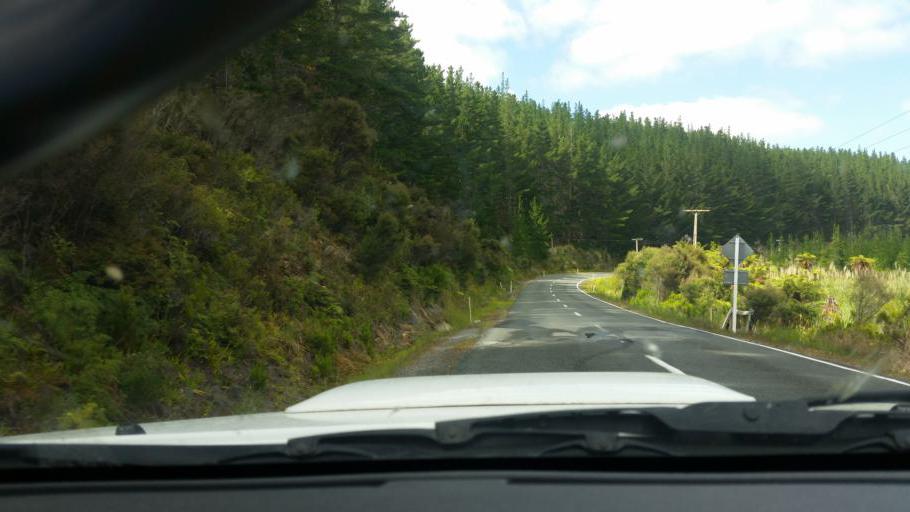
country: NZ
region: Northland
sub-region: Kaipara District
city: Dargaville
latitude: -35.8193
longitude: 173.7108
